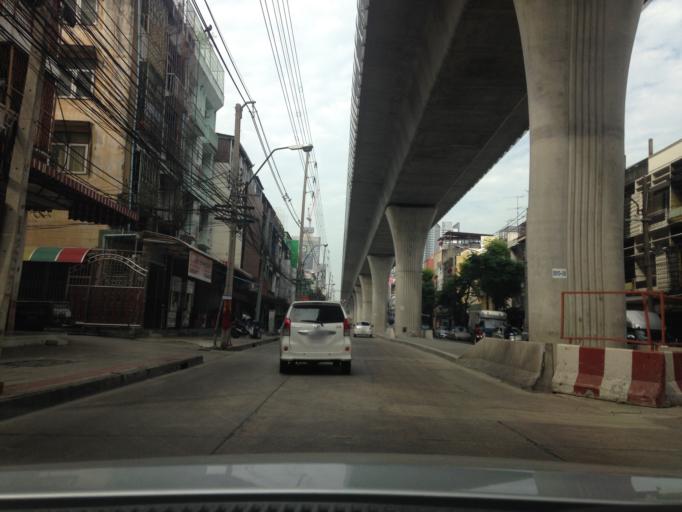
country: TH
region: Bangkok
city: Bang Sue
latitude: 13.8062
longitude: 100.5280
